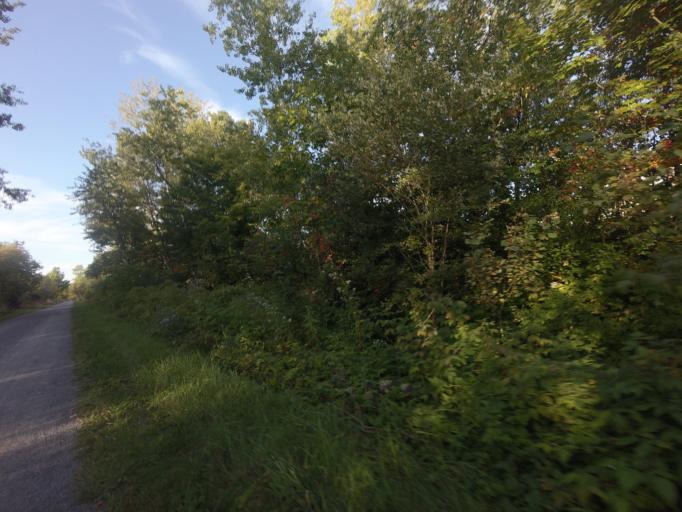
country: CA
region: Quebec
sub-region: Laurentides
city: Prevost
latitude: 45.8417
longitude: -74.0597
